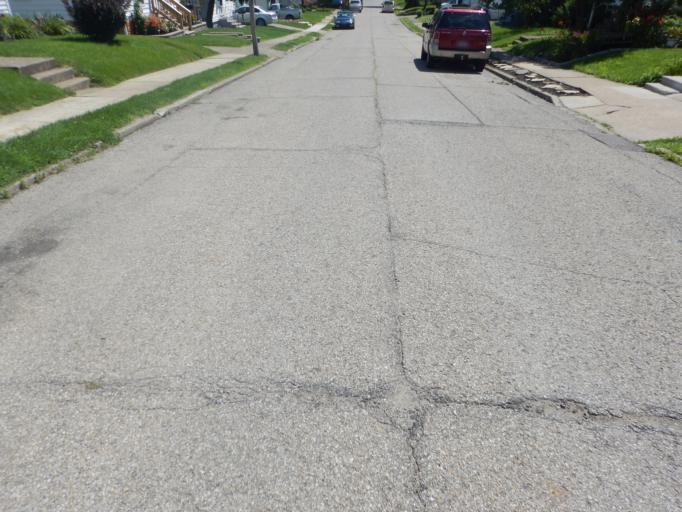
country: US
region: Ohio
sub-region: Muskingum County
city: Zanesville
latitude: 39.9577
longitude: -82.0093
